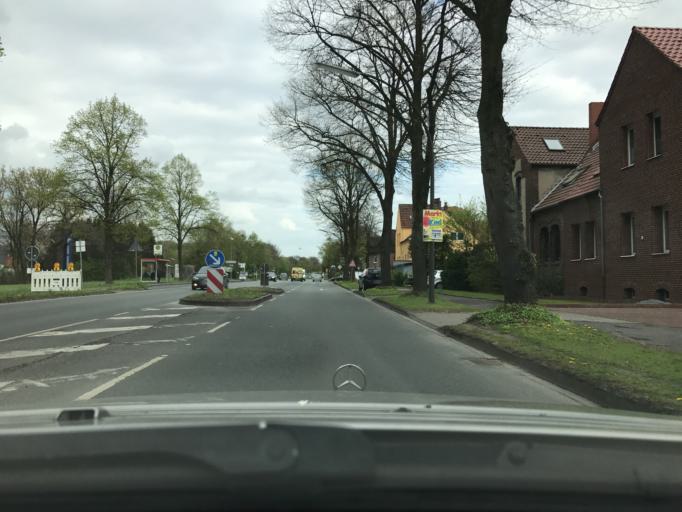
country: DE
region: North Rhine-Westphalia
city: Waltrop
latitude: 51.6217
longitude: 7.4241
